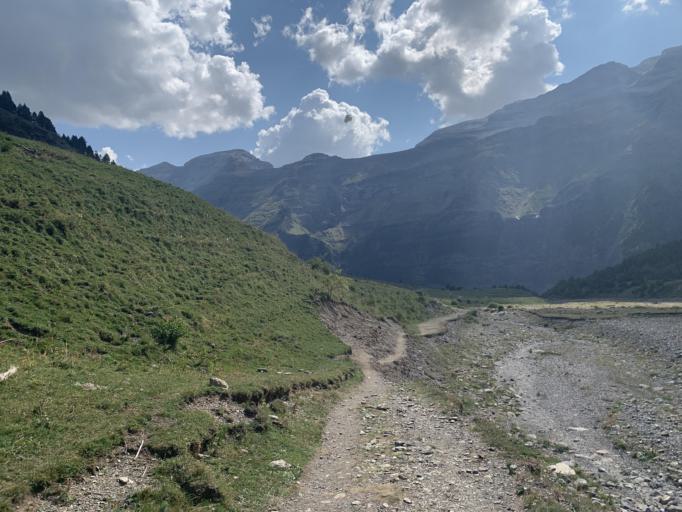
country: ES
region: Aragon
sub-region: Provincia de Huesca
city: Bielsa
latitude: 42.6917
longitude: 0.0886
